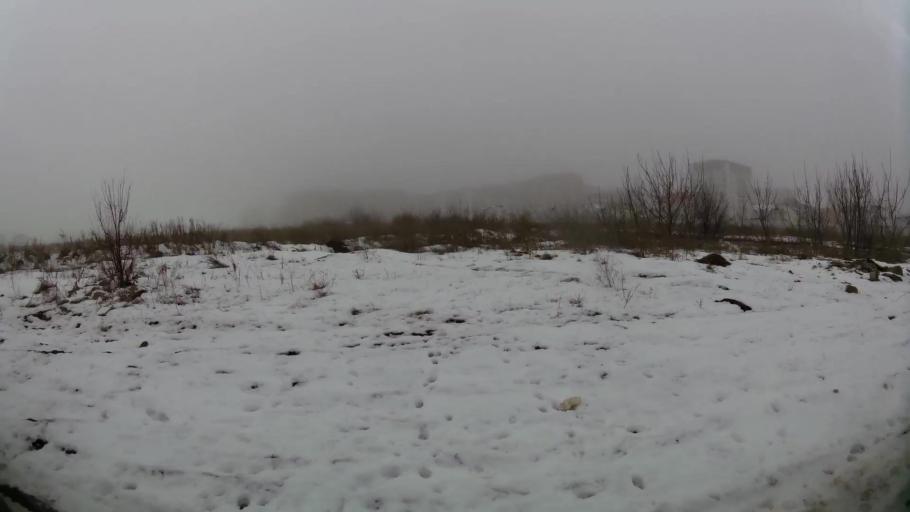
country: RO
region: Ilfov
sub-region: Comuna Chiajna
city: Rosu
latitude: 44.4418
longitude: 25.9934
